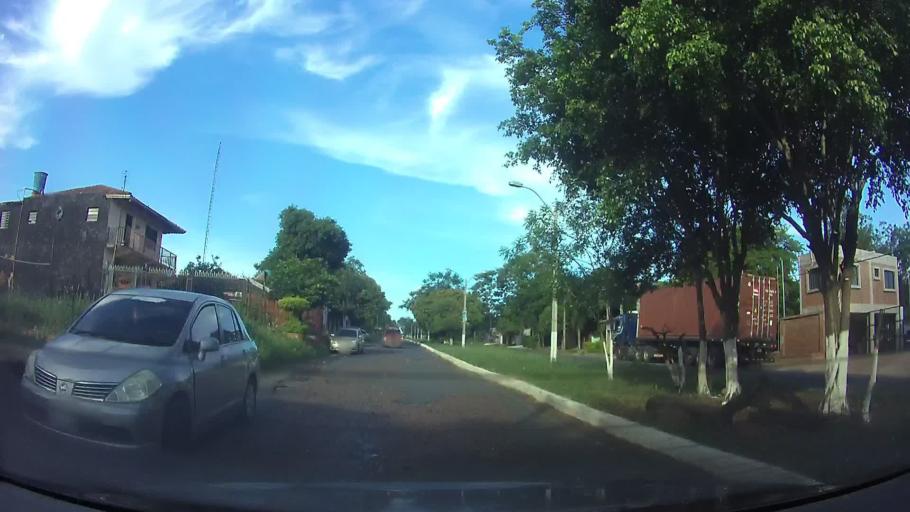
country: PY
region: Central
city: San Antonio
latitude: -25.4314
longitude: -57.5500
